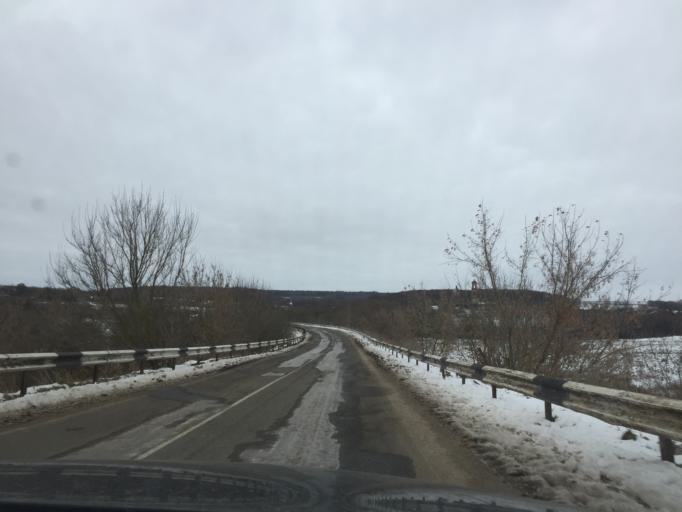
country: RU
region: Tula
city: Teploye
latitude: 53.7755
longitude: 37.6390
